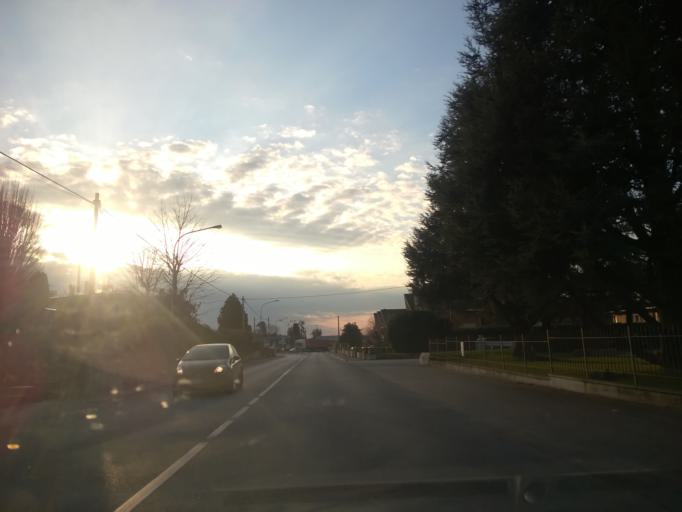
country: IT
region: Veneto
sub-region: Provincia di Vicenza
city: Thiene
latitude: 45.7173
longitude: 11.4691
